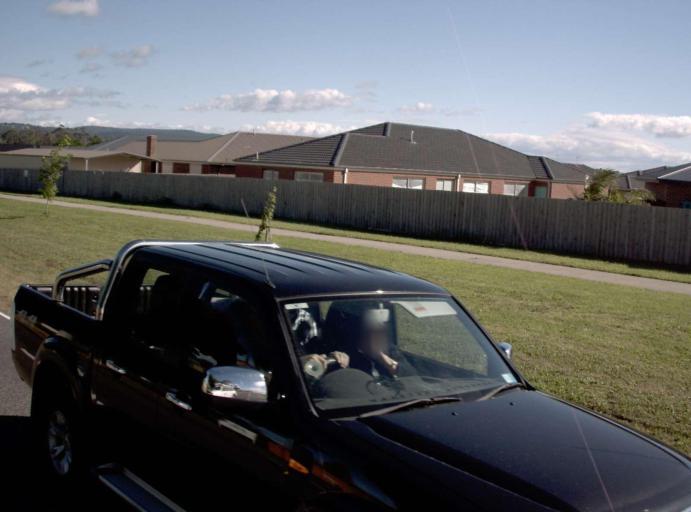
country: AU
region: Victoria
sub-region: Latrobe
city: Traralgon
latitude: -38.1849
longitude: 146.5020
